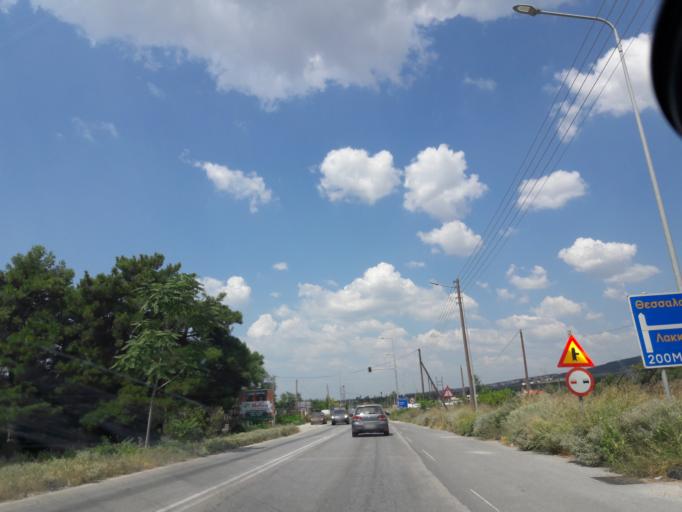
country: GR
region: Central Macedonia
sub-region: Nomos Thessalonikis
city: Souroti
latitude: 40.5050
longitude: 23.0912
